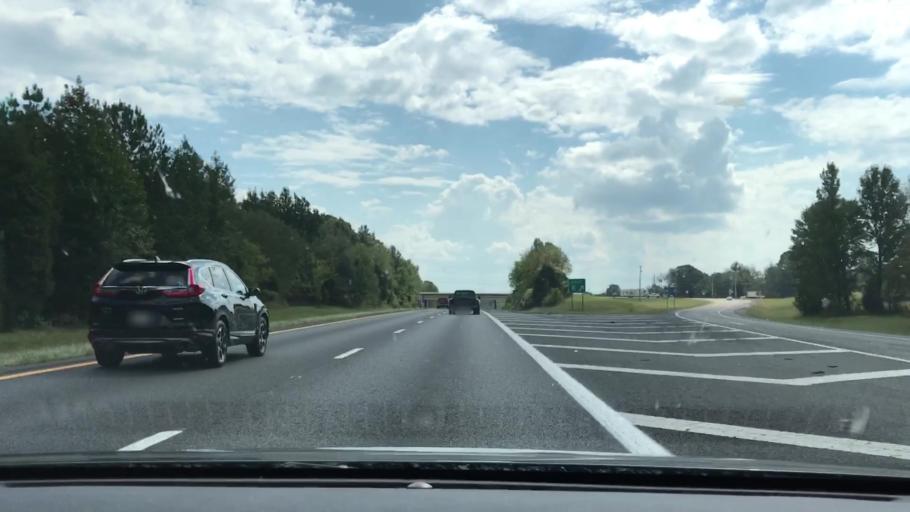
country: US
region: Tennessee
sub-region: Montgomery County
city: Clarksville
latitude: 36.5589
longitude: -87.2517
